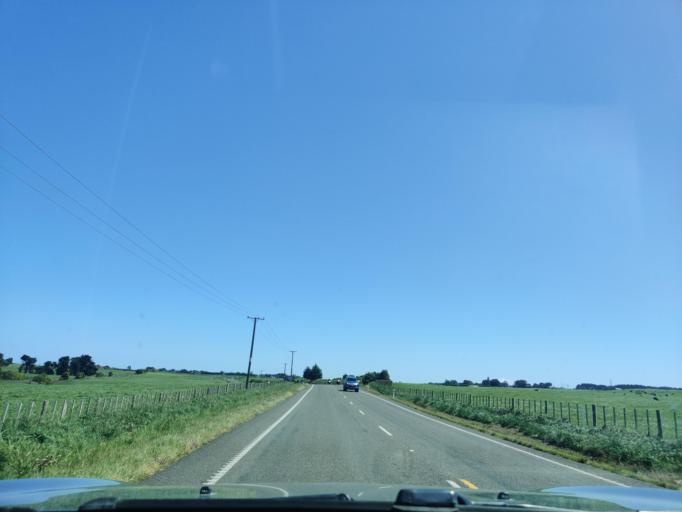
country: NZ
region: Taranaki
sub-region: South Taranaki District
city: Patea
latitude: -39.7717
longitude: 174.6707
